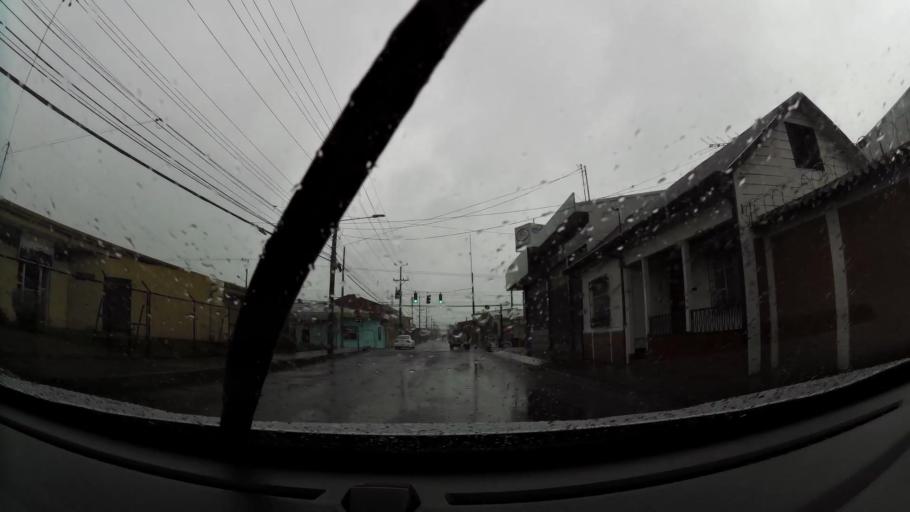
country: CR
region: Cartago
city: Cartago
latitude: 9.8639
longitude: -83.9272
